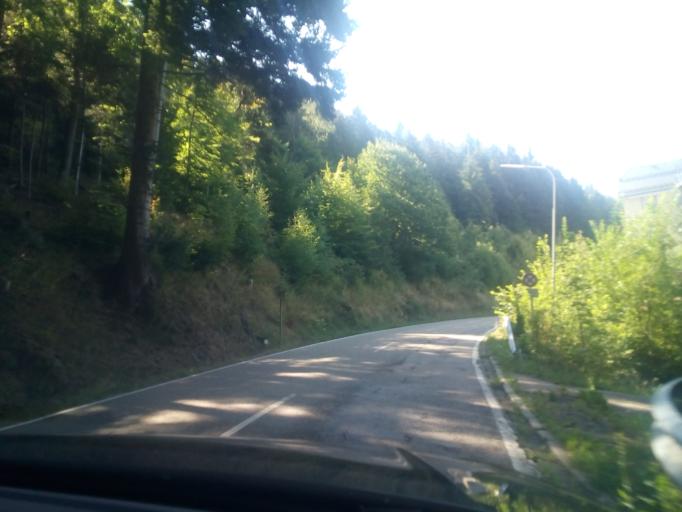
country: DE
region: Baden-Wuerttemberg
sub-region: Karlsruhe Region
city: Buhlertal
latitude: 48.6612
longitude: 8.2204
